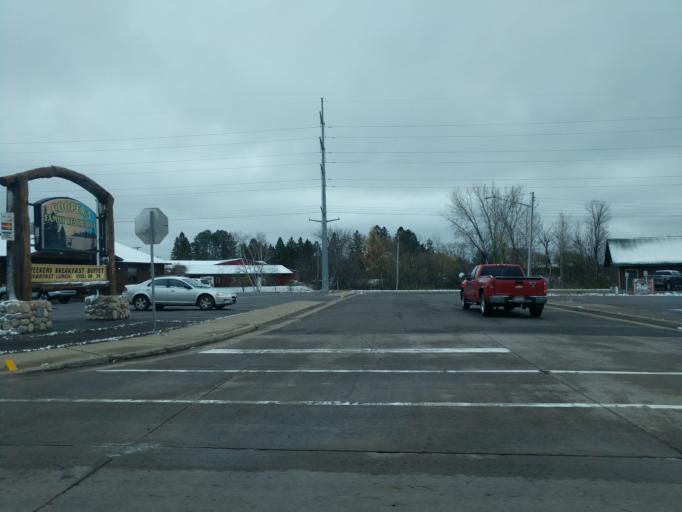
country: US
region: Wisconsin
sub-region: Sawyer County
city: Hayward
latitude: 46.0163
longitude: -91.4796
